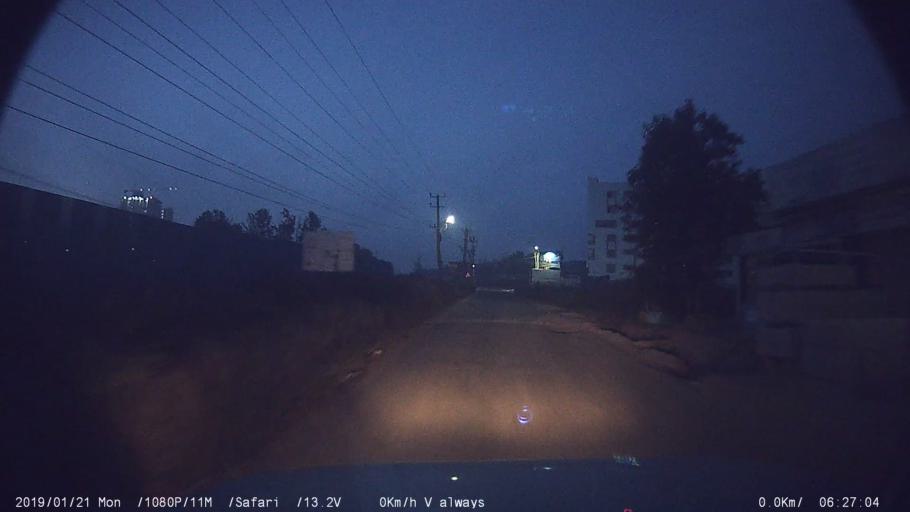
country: IN
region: Karnataka
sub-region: Bangalore Urban
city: Anekal
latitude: 12.8251
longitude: 77.6542
